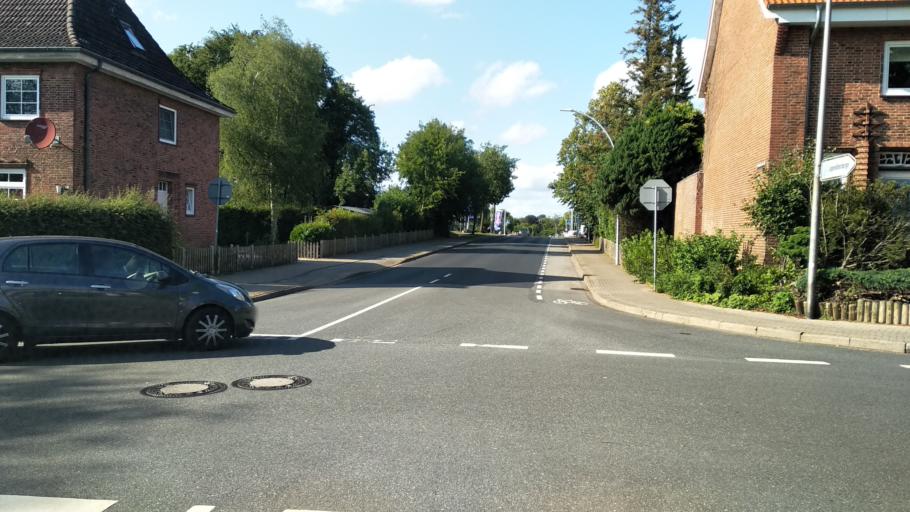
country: DE
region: Schleswig-Holstein
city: Schleswig
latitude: 54.5179
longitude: 9.5516
